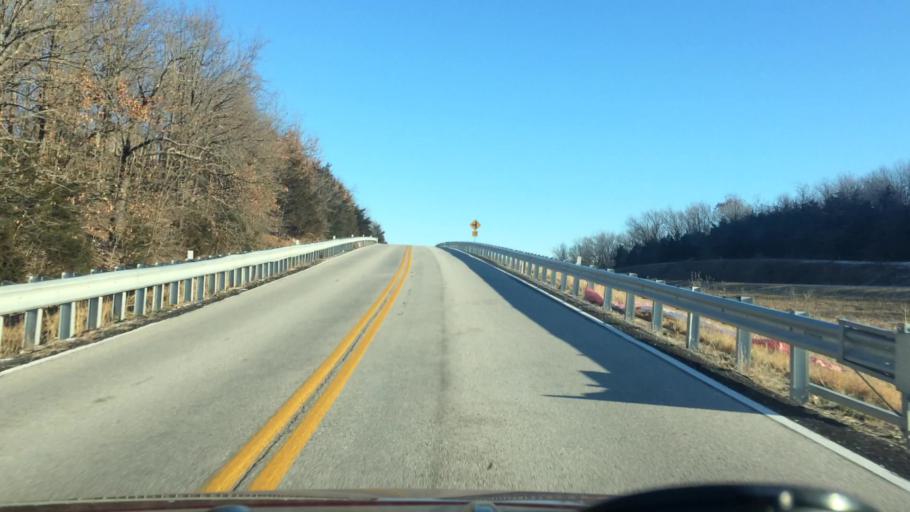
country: US
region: Missouri
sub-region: Greene County
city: Strafford
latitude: 37.2770
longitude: -93.0476
